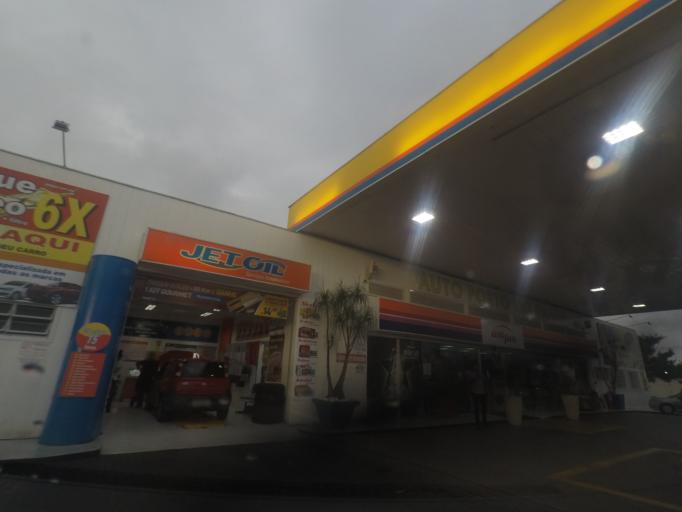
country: BR
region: Parana
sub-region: Curitiba
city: Curitiba
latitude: -25.4706
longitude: -49.3533
